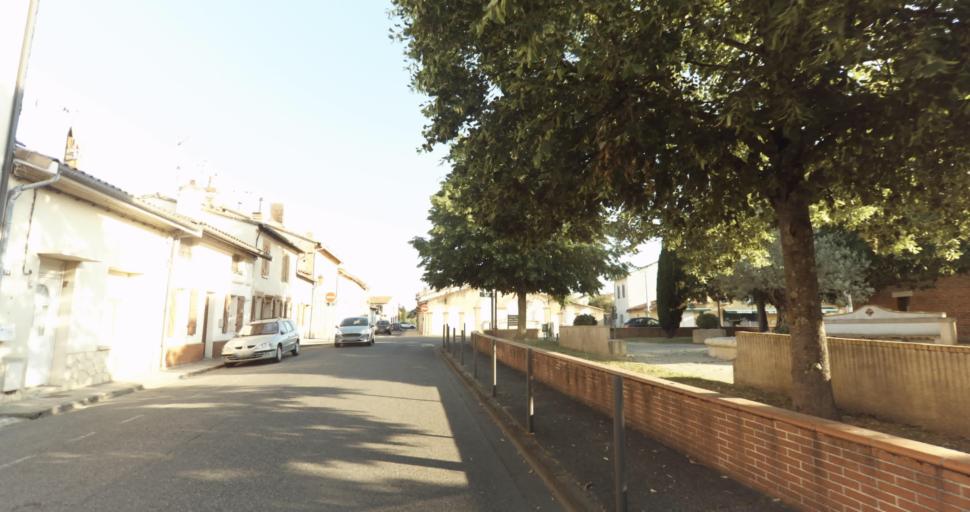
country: FR
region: Midi-Pyrenees
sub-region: Departement de la Haute-Garonne
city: Leguevin
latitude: 43.5986
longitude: 1.2335
